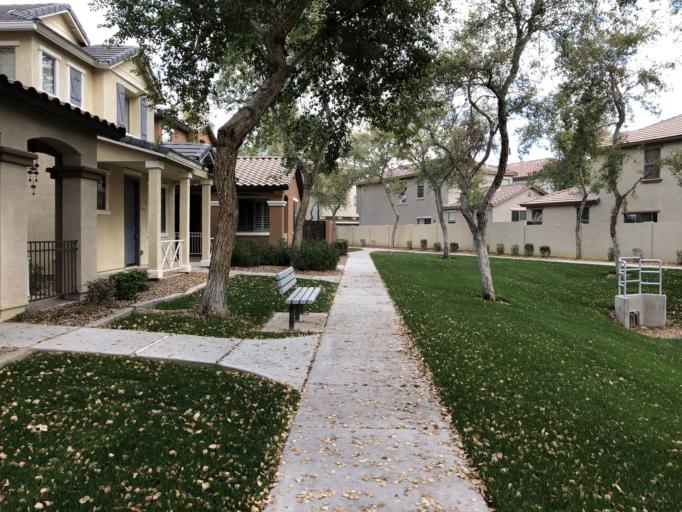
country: US
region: Arizona
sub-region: Maricopa County
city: Queen Creek
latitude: 33.2792
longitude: -111.7084
